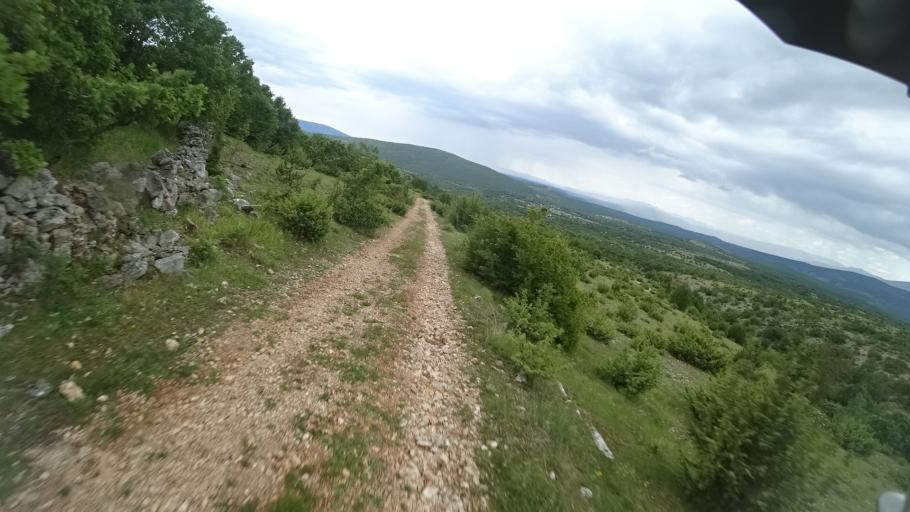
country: HR
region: Sibensko-Kniniska
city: Knin
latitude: 43.9864
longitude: 16.3225
